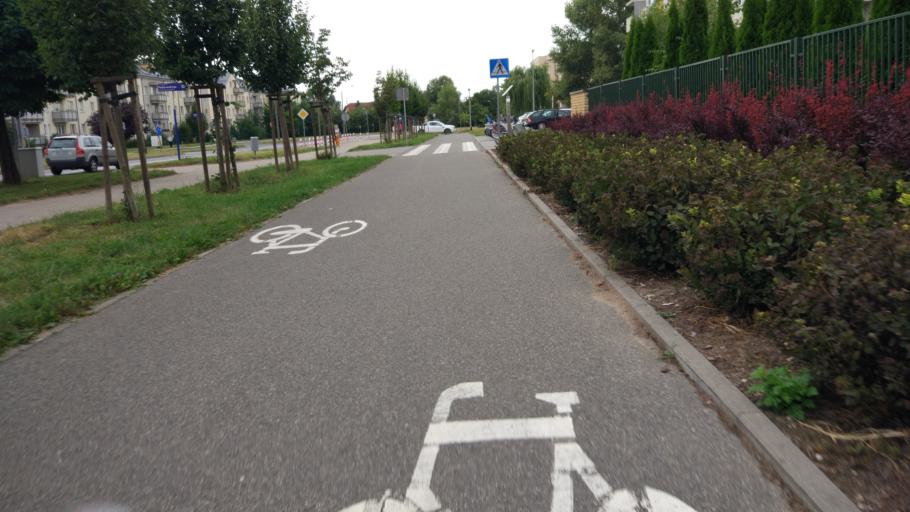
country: PL
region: Masovian Voivodeship
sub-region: Plock
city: Plock
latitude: 52.5306
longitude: 19.7523
